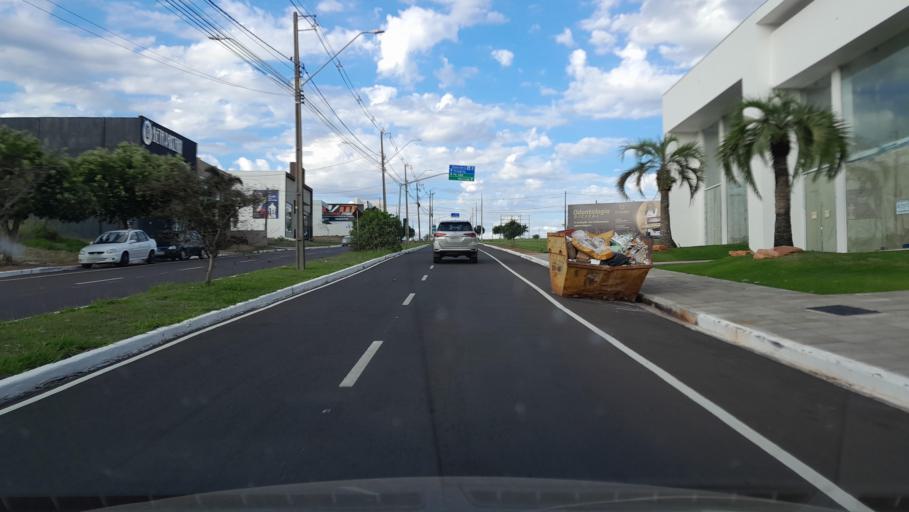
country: BR
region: Parana
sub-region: Umuarama
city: Umuarama
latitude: -23.7530
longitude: -53.2755
